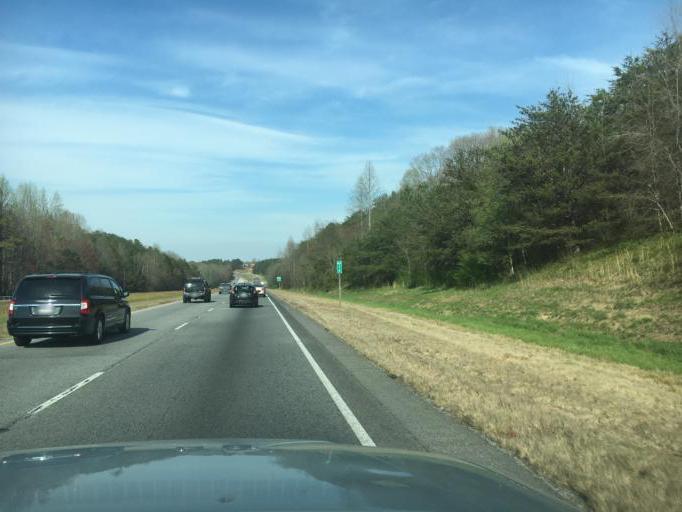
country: US
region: Georgia
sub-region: Hall County
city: Lula
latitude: 34.4105
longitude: -83.6658
